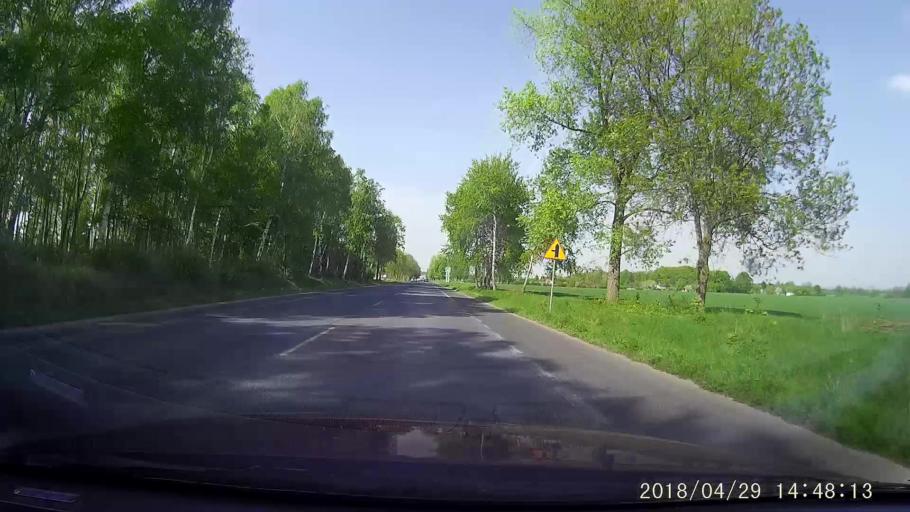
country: PL
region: Lower Silesian Voivodeship
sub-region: Powiat zgorzelecki
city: Zgorzelec
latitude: 51.1182
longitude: 15.0146
